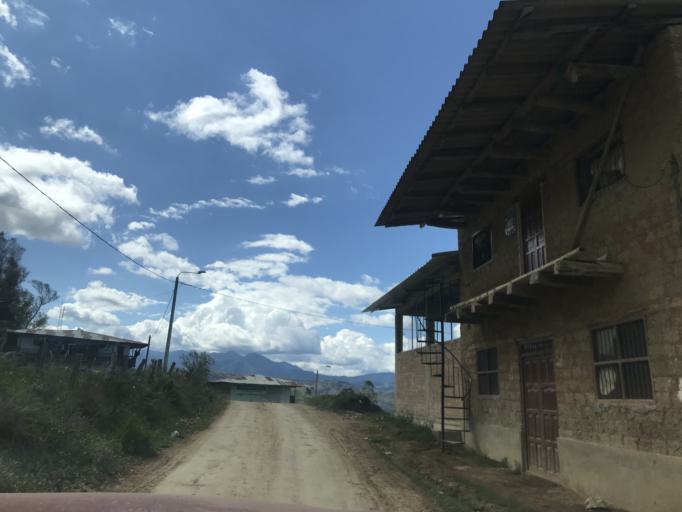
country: PE
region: Cajamarca
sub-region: Provincia de Chota
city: Querocoto
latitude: -6.3349
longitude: -79.0686
